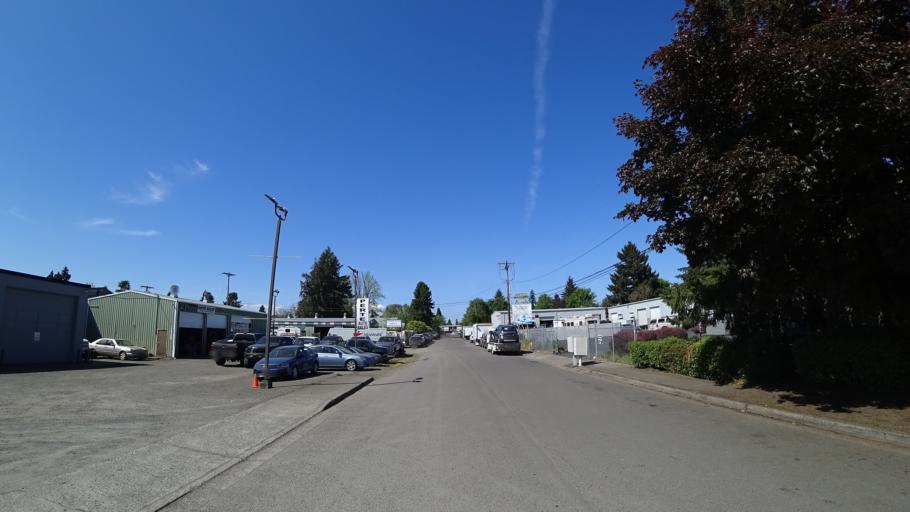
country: US
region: Oregon
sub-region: Washington County
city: Hillsboro
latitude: 45.5087
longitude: -122.9644
